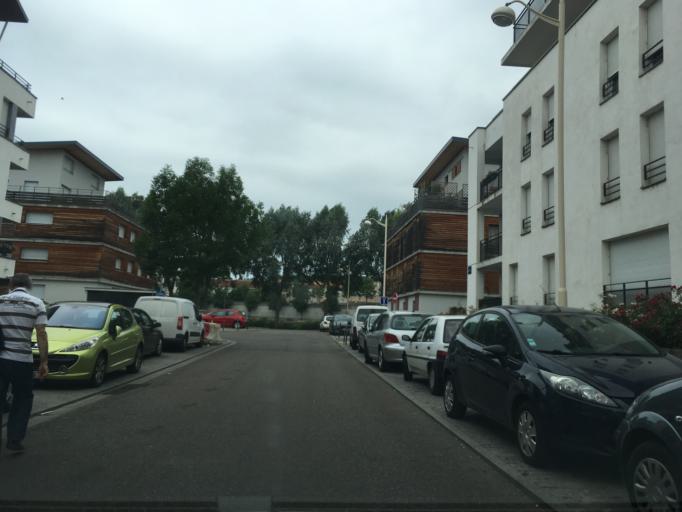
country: FR
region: Lorraine
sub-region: Departement de Meurthe-et-Moselle
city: Saint-Max
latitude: 48.6990
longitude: 6.2007
